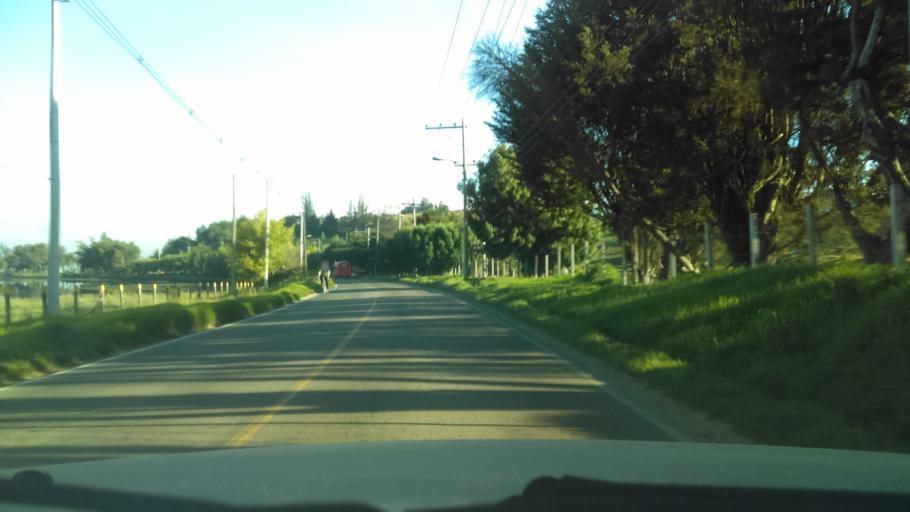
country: CO
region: Cundinamarca
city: Sibate
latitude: 4.5119
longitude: -74.2441
